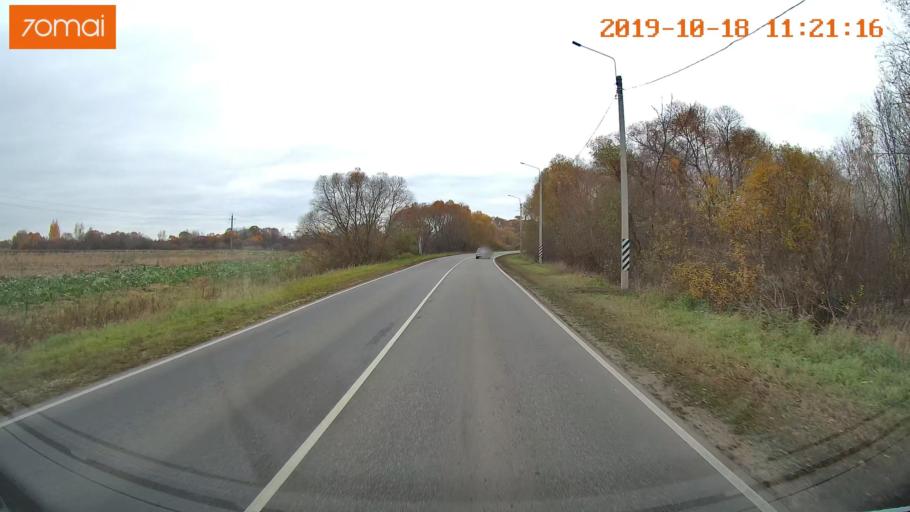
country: RU
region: Tula
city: Kimovsk
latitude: 54.0720
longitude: 38.5632
